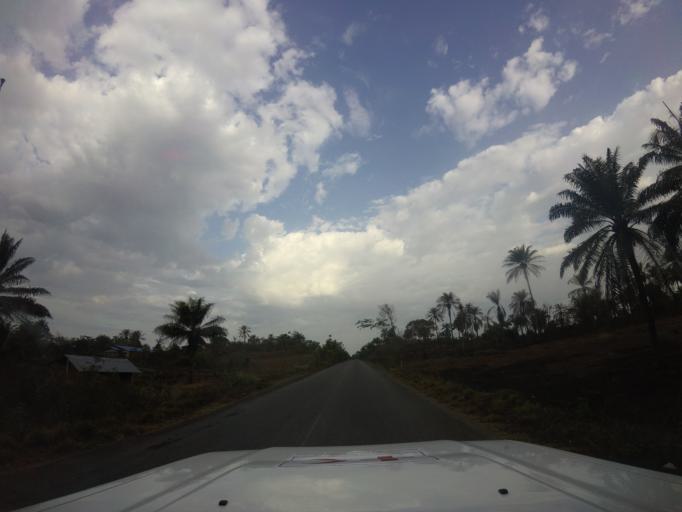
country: LR
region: Bomi
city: Tubmanburg
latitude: 6.6990
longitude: -10.9113
